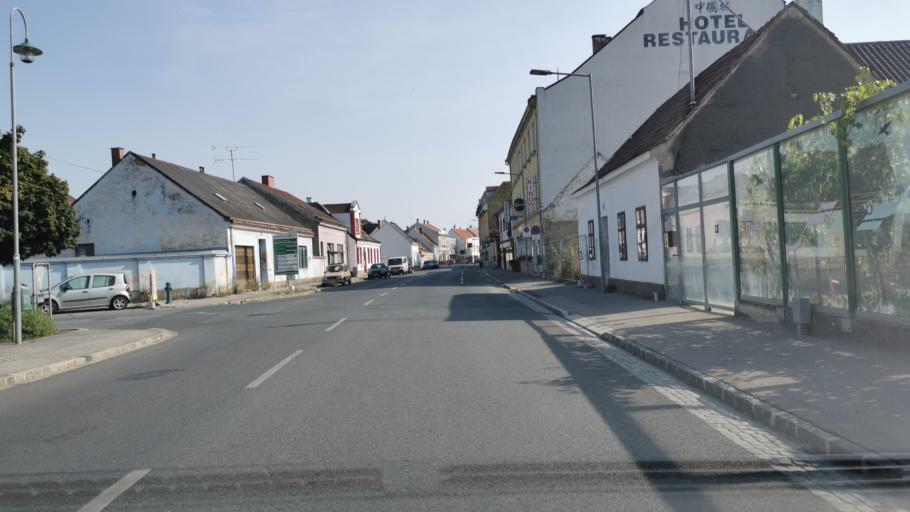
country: AT
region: Lower Austria
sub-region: Politischer Bezirk Mistelbach
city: Mistelbach
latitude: 48.5726
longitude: 16.5719
